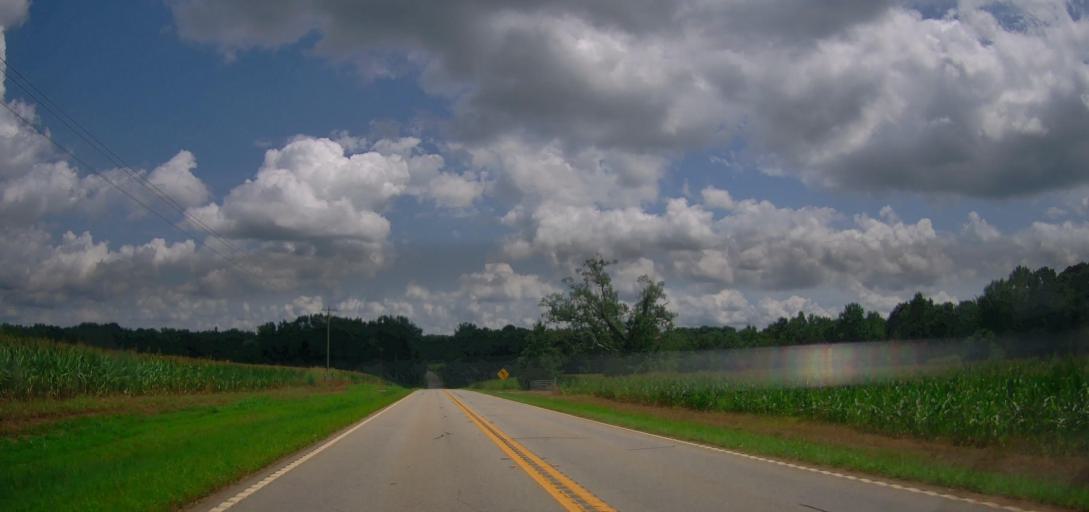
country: US
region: Georgia
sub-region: Heard County
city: Franklin
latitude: 33.3476
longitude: -85.1880
